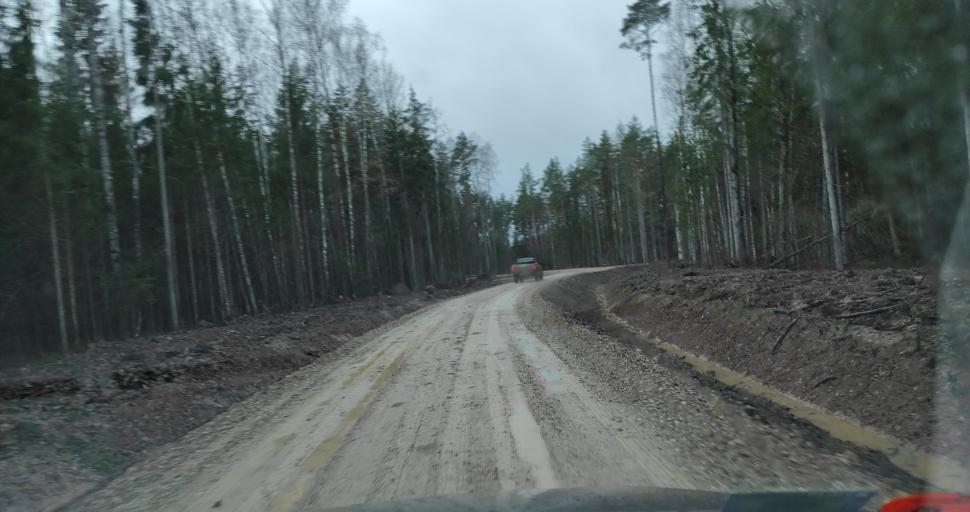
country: LV
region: Skrunda
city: Skrunda
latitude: 56.5585
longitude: 22.0521
